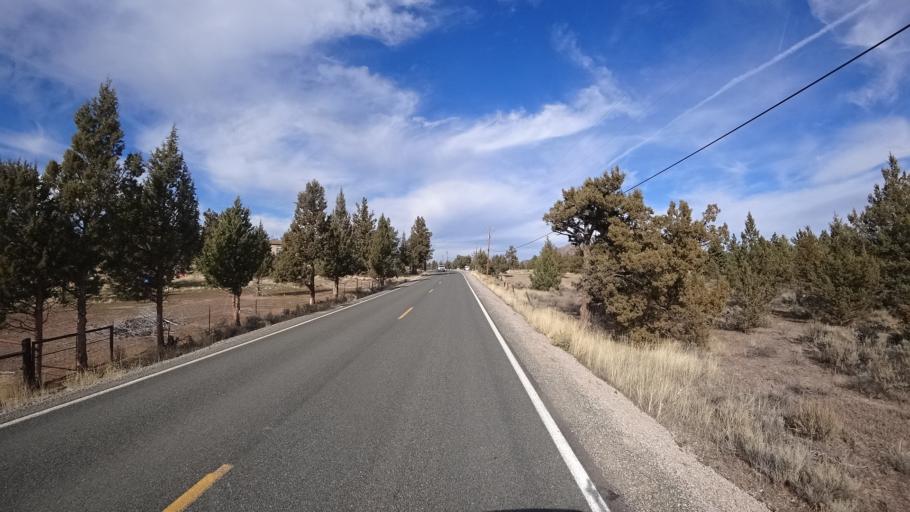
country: US
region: California
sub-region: Siskiyou County
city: Montague
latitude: 41.6462
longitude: -122.3987
